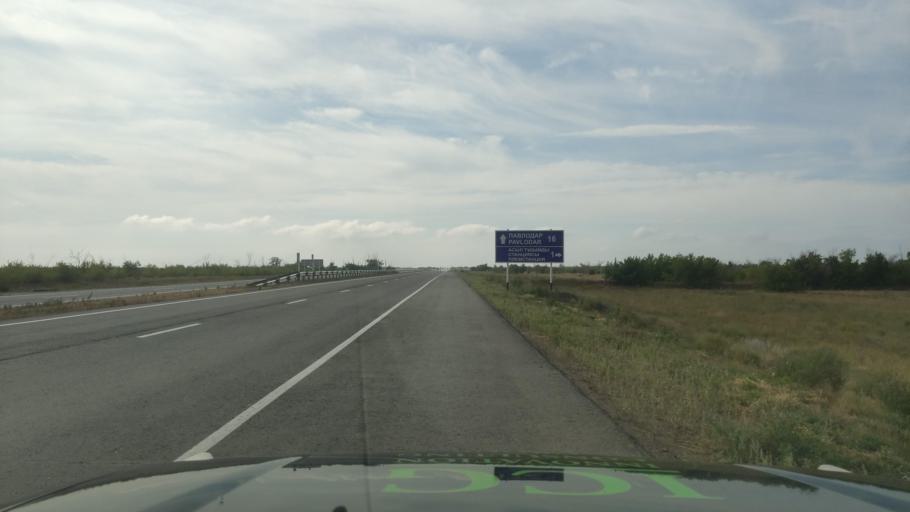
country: KZ
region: Pavlodar
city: Leninskiy
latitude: 52.4986
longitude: 76.8297
